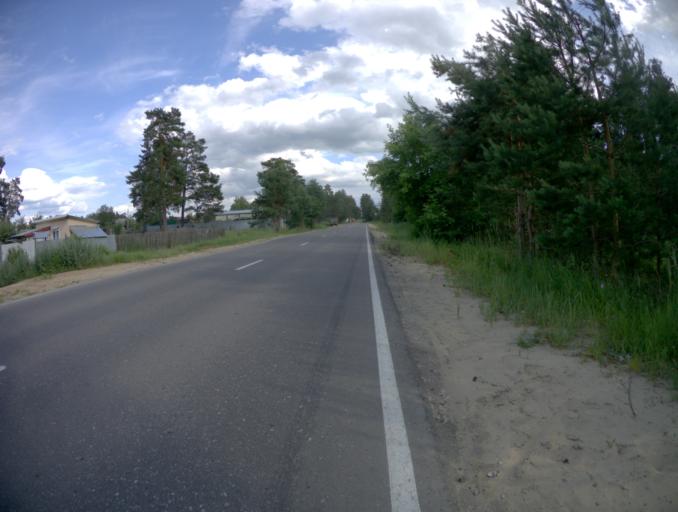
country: RU
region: Vladimir
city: Gorokhovets
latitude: 56.2946
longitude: 42.7822
